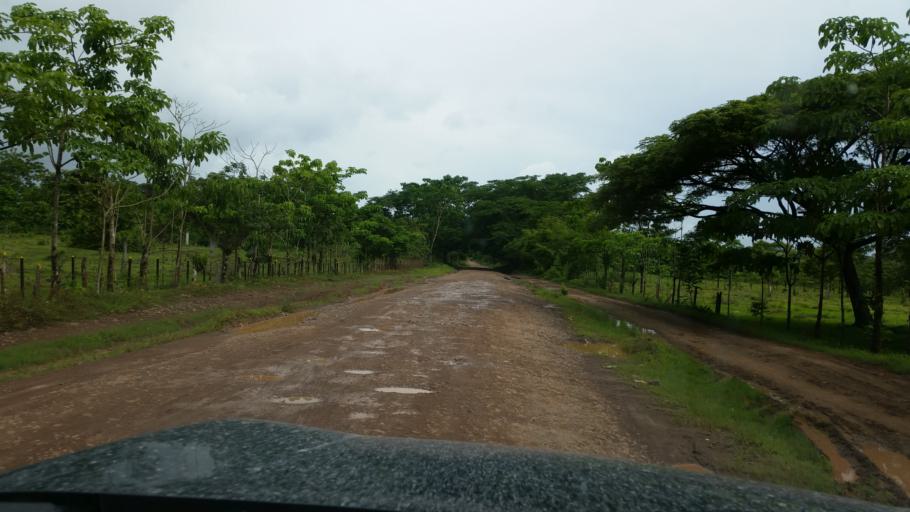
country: NI
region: Atlantico Norte (RAAN)
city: Siuna
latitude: 13.4279
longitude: -84.8526
